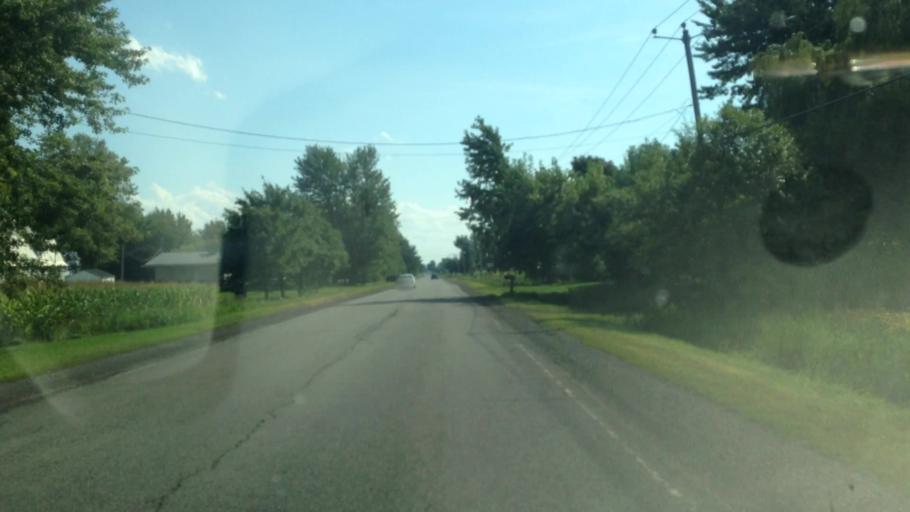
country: CA
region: Quebec
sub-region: Monteregie
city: Mercier
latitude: 45.2815
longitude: -73.6897
